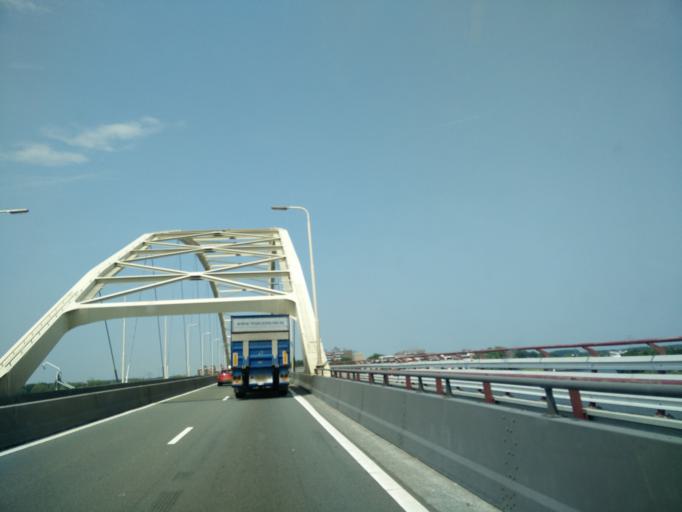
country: NL
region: South Holland
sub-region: Gemeente Papendrecht
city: Papendrecht
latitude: 51.8218
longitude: 4.7061
